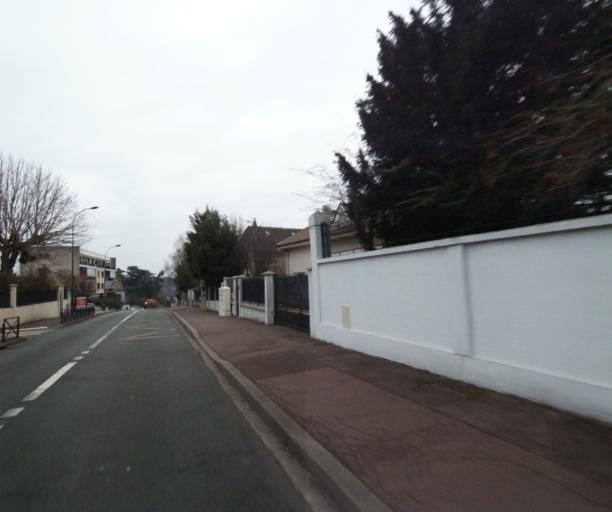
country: FR
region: Ile-de-France
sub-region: Departement des Hauts-de-Seine
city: Vaucresson
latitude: 48.8340
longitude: 2.1540
